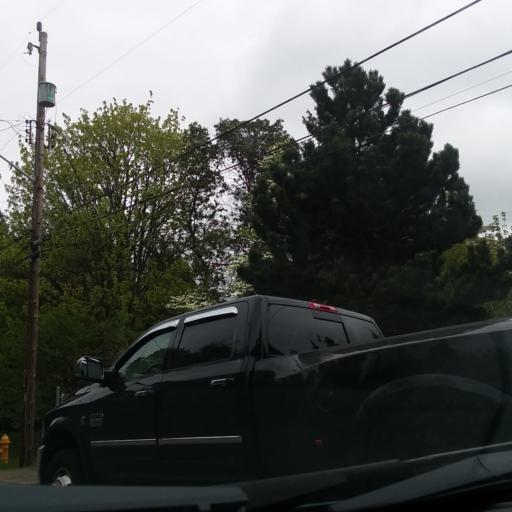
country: US
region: Washington
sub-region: King County
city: Boulevard Park
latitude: 47.5008
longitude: -122.3265
